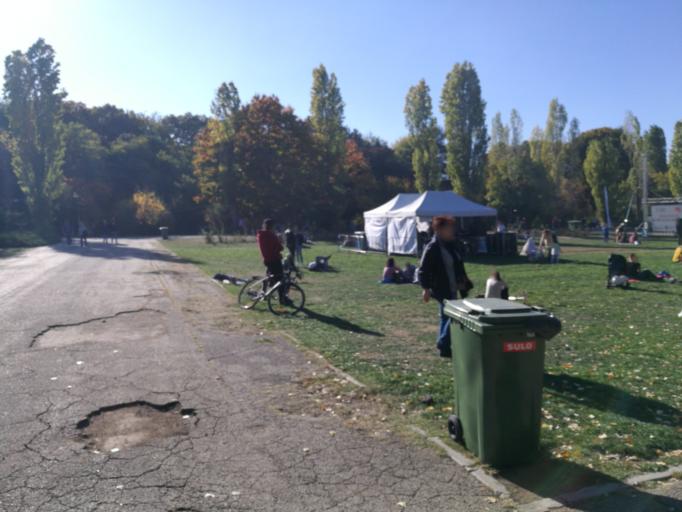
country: RO
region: Bucuresti
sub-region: Municipiul Bucuresti
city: Bucuresti
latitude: 44.4690
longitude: 26.0843
